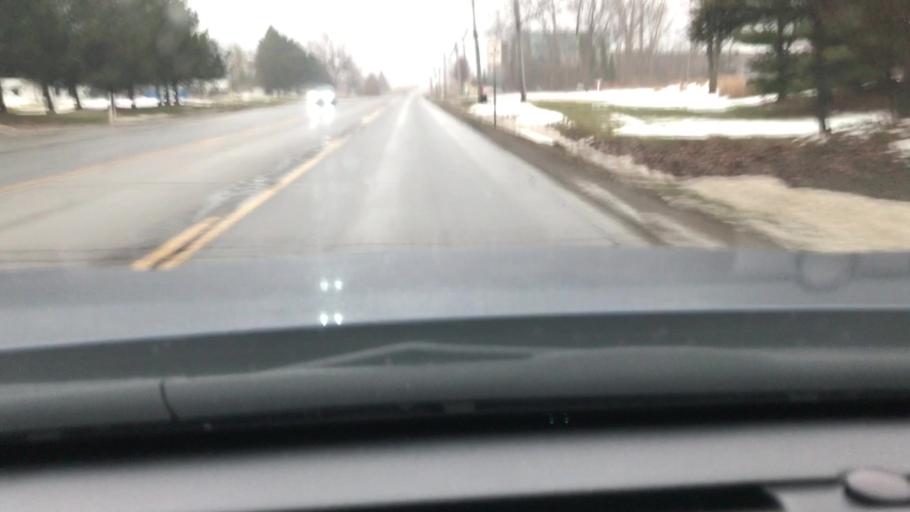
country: US
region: Michigan
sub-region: Oakland County
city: Wixom
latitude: 42.5025
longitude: -83.5162
